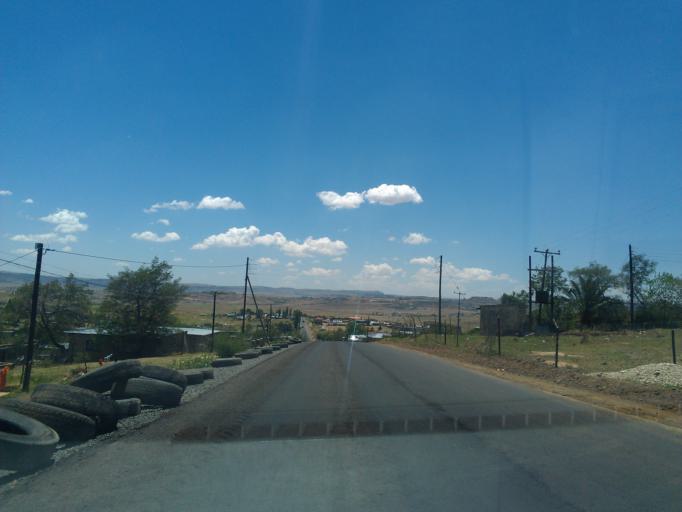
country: LS
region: Berea
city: Teyateyaneng
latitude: -29.1453
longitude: 27.7594
